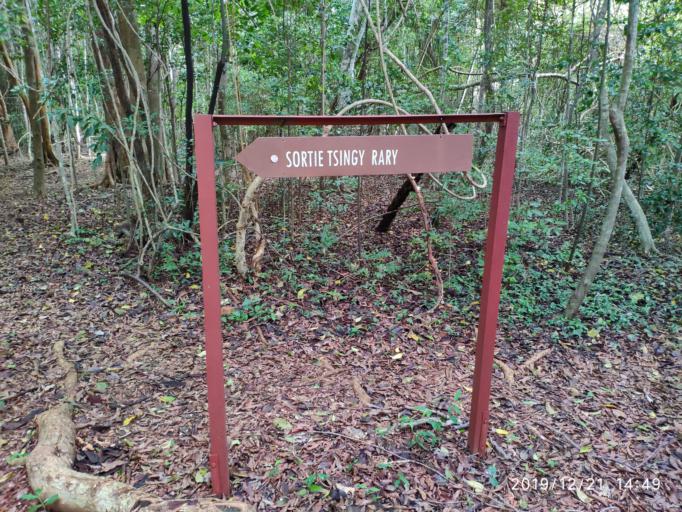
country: MG
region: Diana
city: Ambilobe
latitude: -12.9400
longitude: 49.1209
